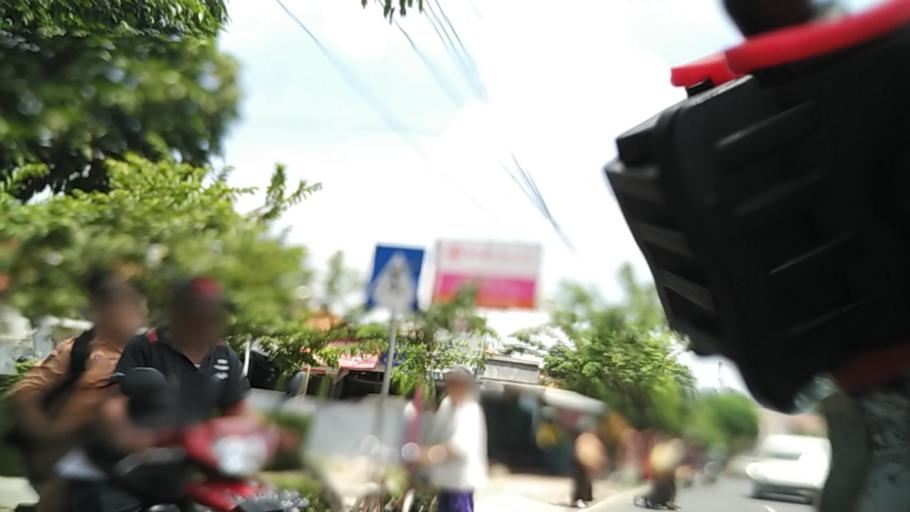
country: ID
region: Central Java
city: Semarang
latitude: -7.0089
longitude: 110.3860
